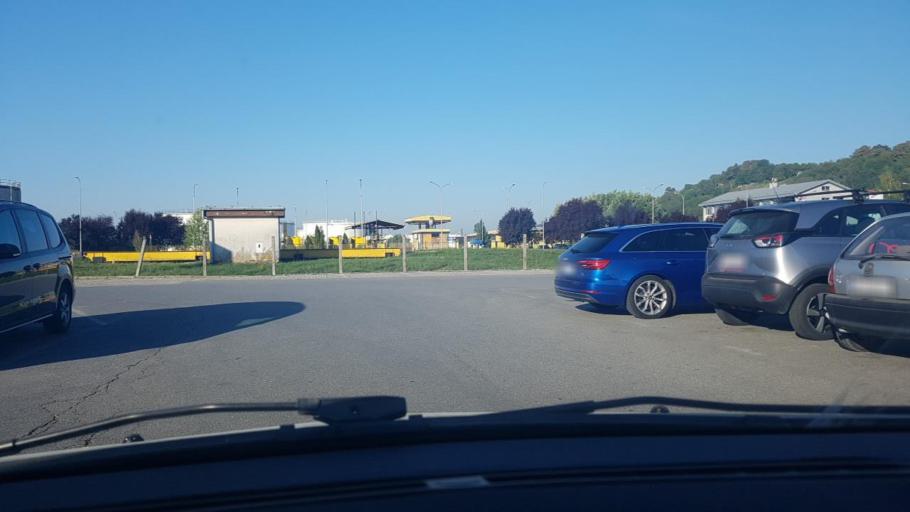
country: HR
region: Krapinsko-Zagorska
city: Zabok
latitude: 46.0215
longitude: 15.9023
